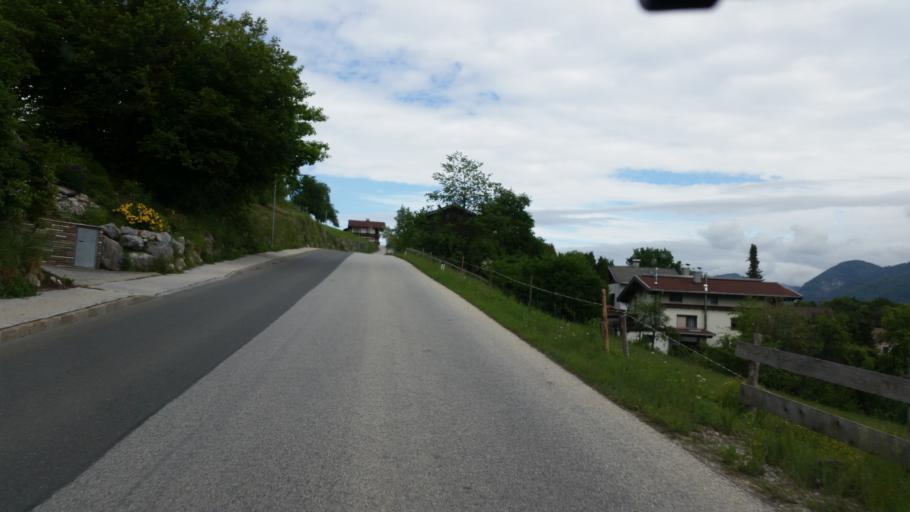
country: AT
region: Tyrol
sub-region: Politischer Bezirk Kufstein
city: Breitenbach am Inn
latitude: 47.4837
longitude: 11.9840
